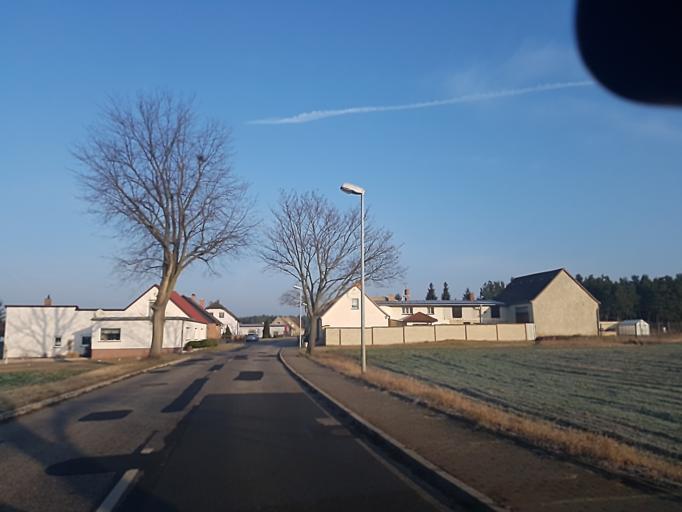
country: DE
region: Brandenburg
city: Bruck
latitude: 52.2303
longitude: 12.7134
